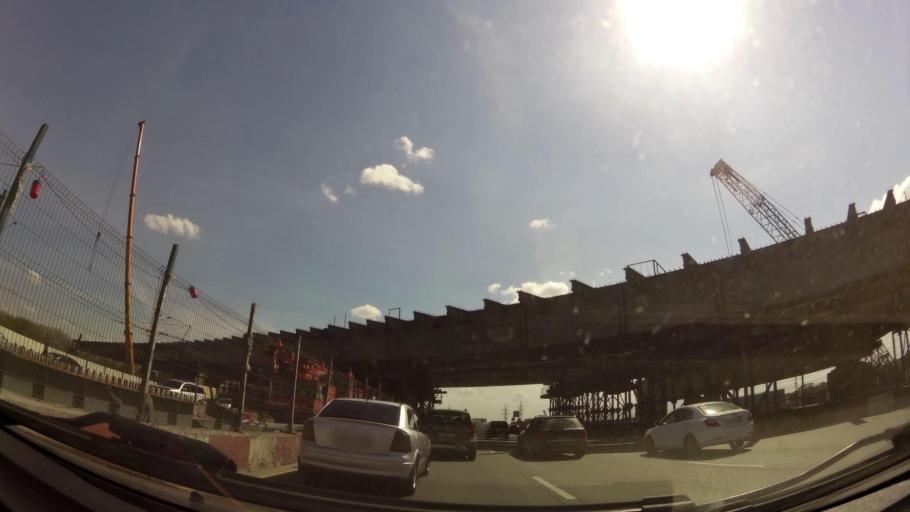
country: RU
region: Moskovskaya
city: Nemchinovka
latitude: 55.7293
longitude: 37.3778
